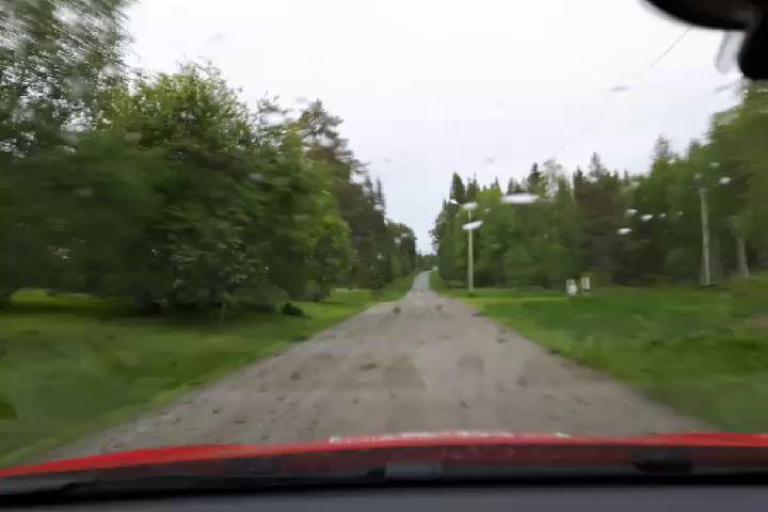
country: SE
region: Jaemtland
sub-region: Bergs Kommun
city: Hoverberg
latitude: 62.7496
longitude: 14.4481
